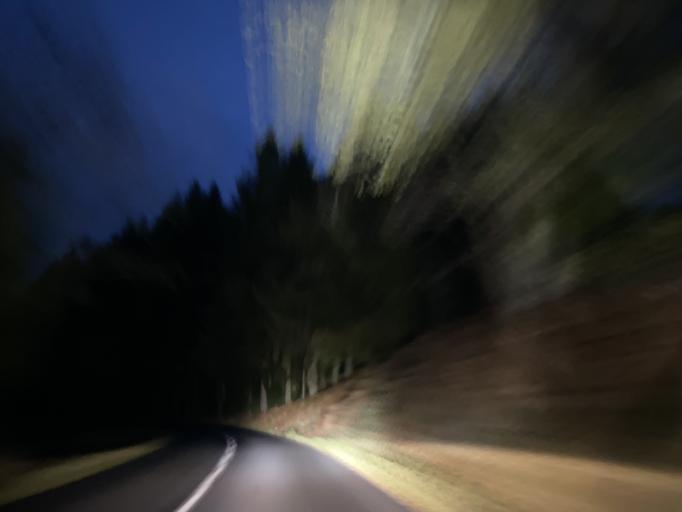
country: FR
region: Auvergne
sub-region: Departement du Puy-de-Dome
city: Cunlhat
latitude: 45.6065
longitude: 3.5151
